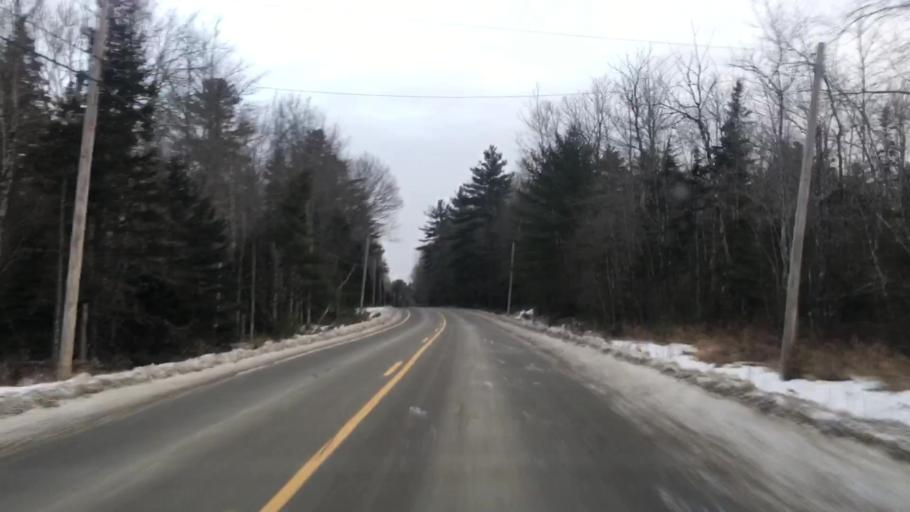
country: US
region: Maine
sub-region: Hancock County
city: Ellsworth
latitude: 44.6206
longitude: -68.3825
